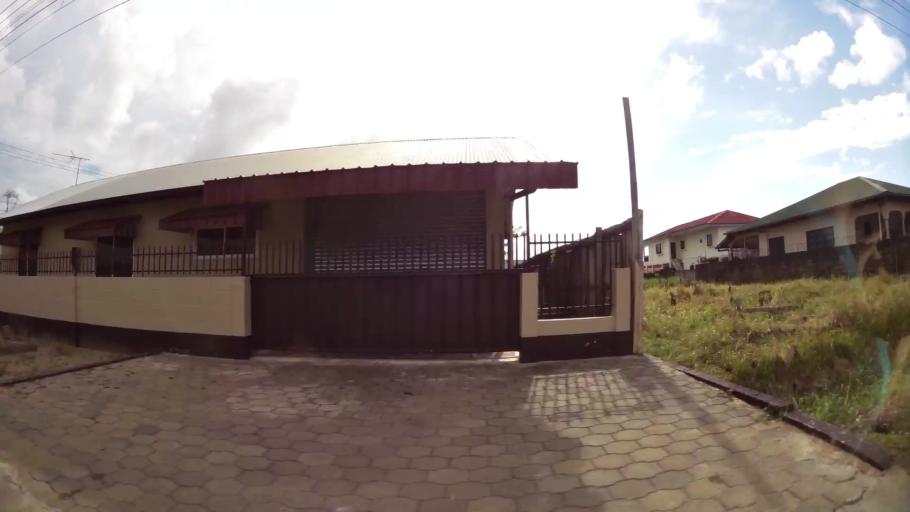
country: SR
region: Paramaribo
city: Paramaribo
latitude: 5.8564
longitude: -55.1795
